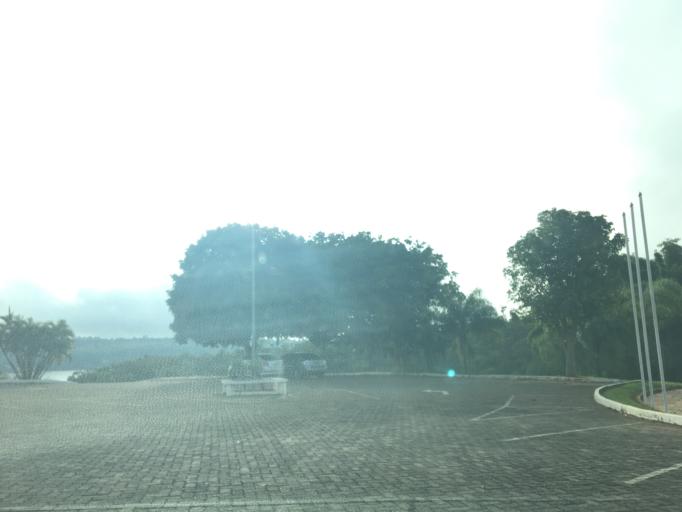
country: BR
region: Federal District
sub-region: Brasilia
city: Brasilia
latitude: -15.7971
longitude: -47.7994
